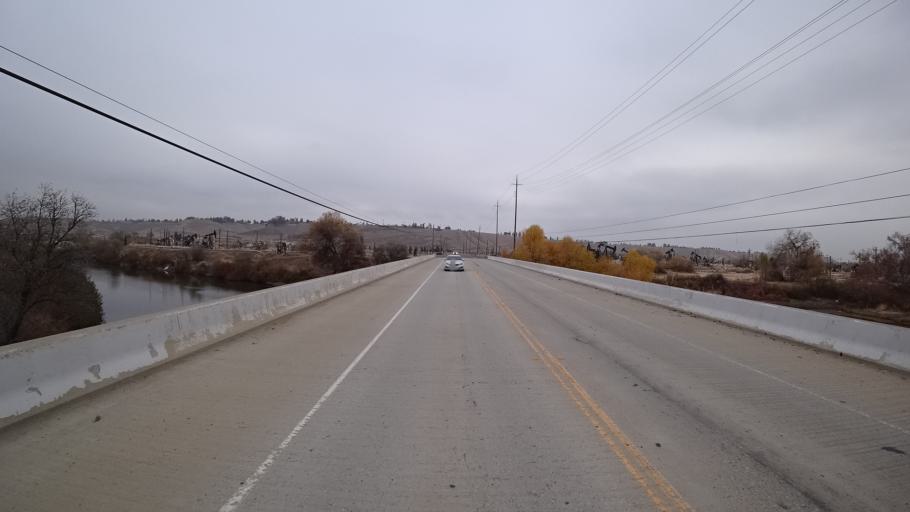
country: US
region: California
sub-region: Kern County
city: Oildale
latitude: 35.4260
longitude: -118.9677
